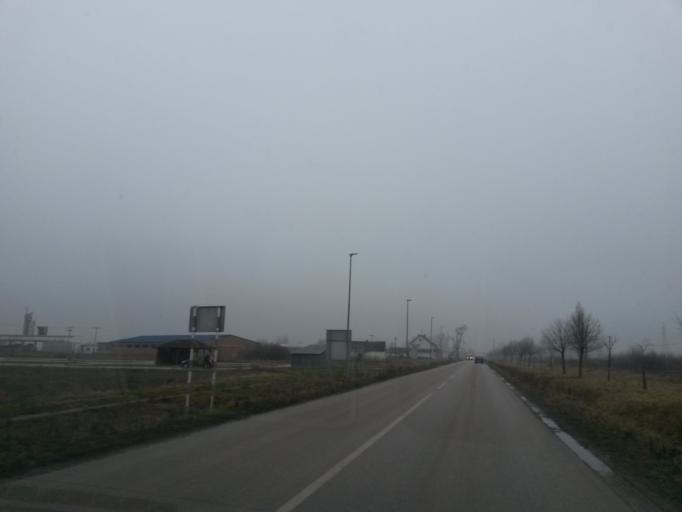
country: HR
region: Vukovarsko-Srijemska
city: Zupanja
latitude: 45.0964
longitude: 18.6978
